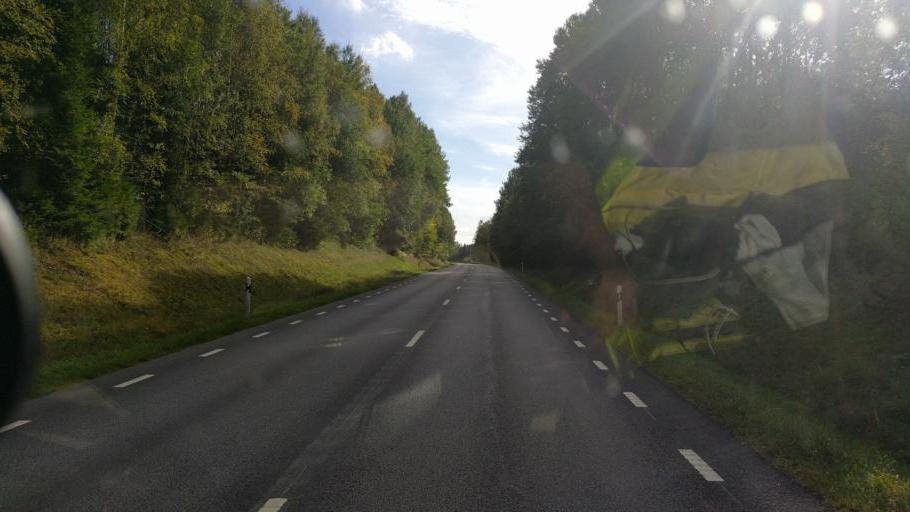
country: SE
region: OEstergoetland
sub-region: Kinda Kommun
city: Kisa
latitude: 57.9384
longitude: 15.6678
